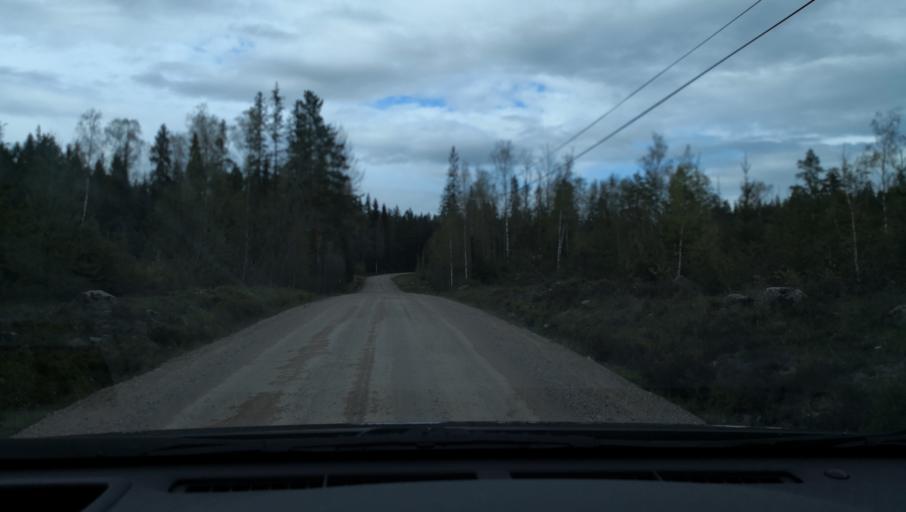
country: SE
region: Vaestmanland
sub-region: Fagersta Kommun
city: Fagersta
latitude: 60.1026
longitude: 15.7933
